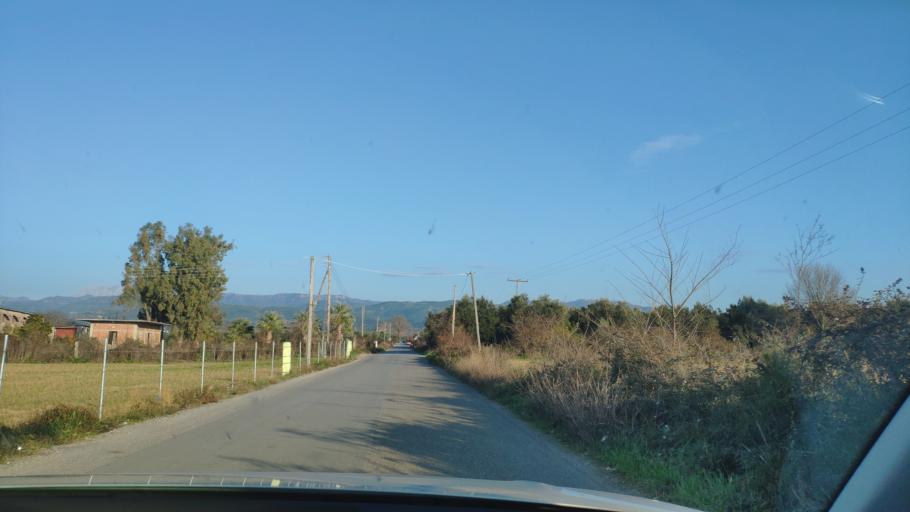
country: GR
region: West Greece
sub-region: Nomos Aitolias kai Akarnanias
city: Krikellos
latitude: 38.9296
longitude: 21.1531
